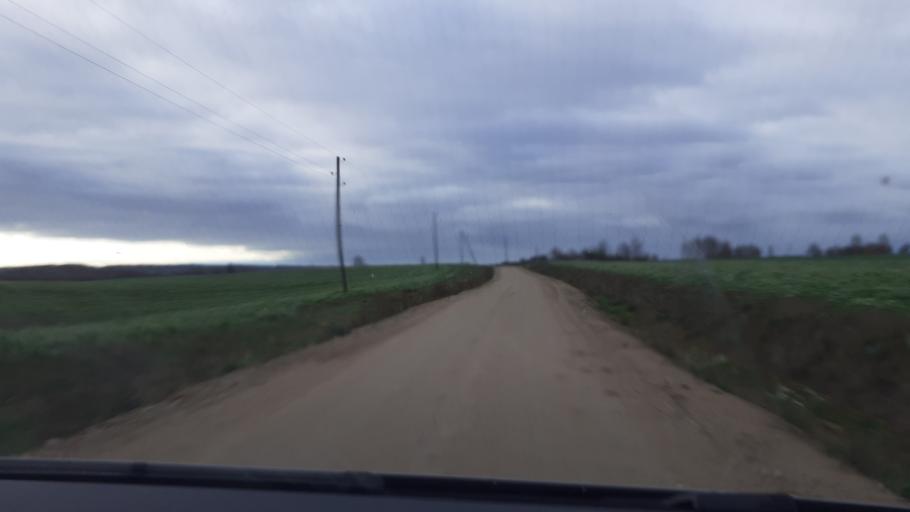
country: LV
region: Aizpute
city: Aizpute
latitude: 56.7677
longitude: 21.8041
